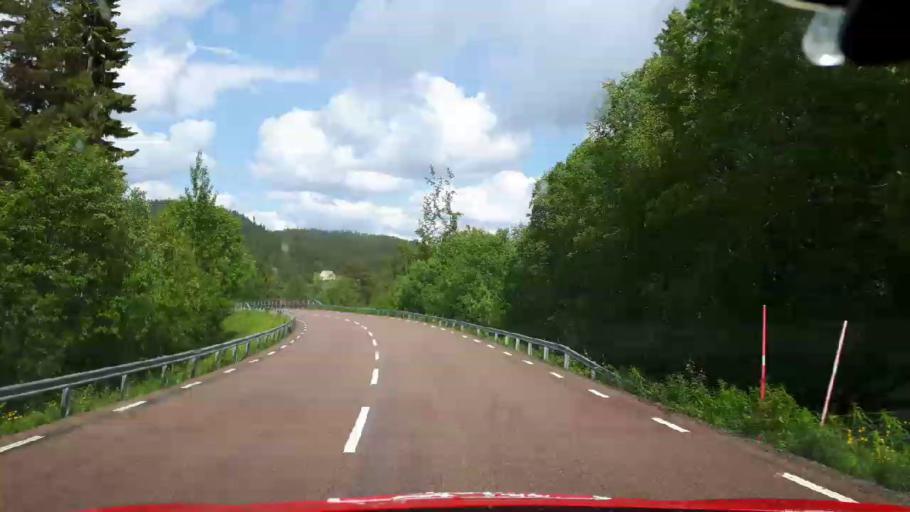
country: SE
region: Jaemtland
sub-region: Krokoms Kommun
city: Valla
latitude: 63.9703
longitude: 14.1634
